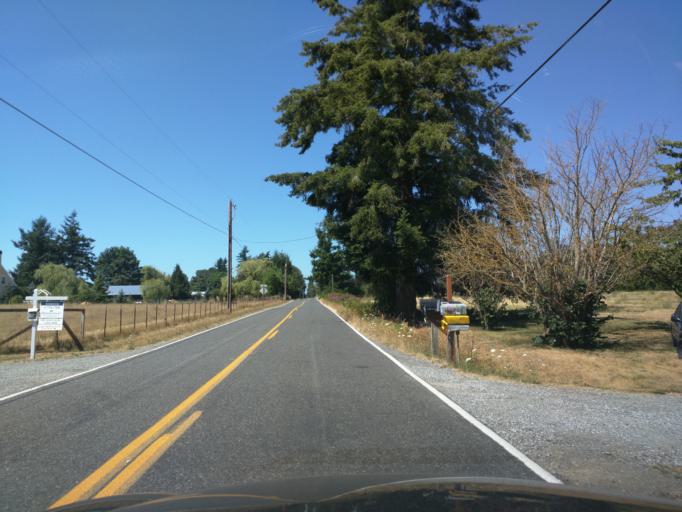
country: US
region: Washington
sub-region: Whatcom County
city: Lynden
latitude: 48.8772
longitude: -122.4155
